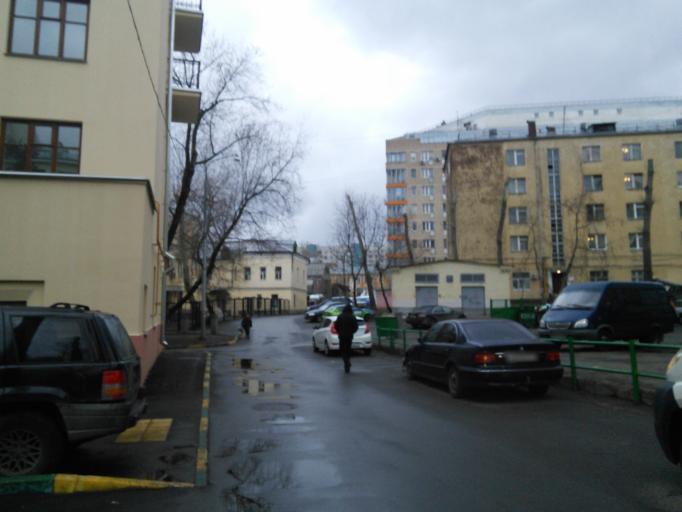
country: RU
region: Moskovskaya
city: Bogorodskoye
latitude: 55.7907
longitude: 37.7136
